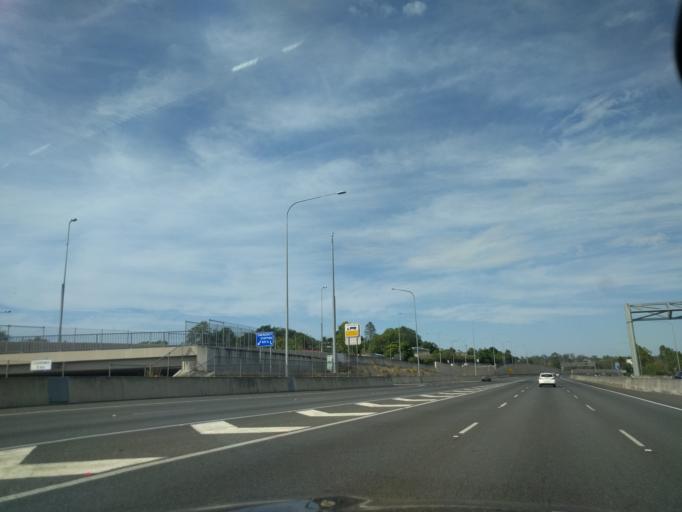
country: AU
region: Queensland
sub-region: Brisbane
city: Wacol
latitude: -27.6071
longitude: 152.9134
